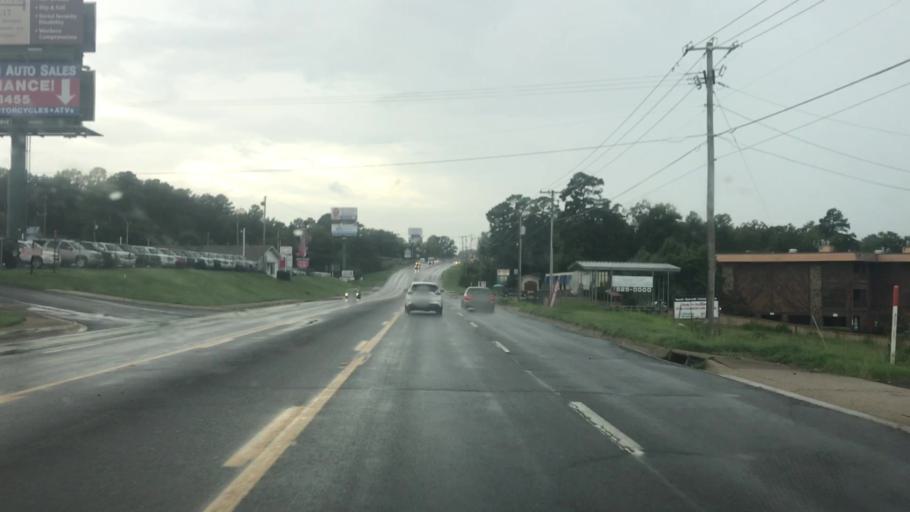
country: US
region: Arkansas
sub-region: Garland County
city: Rockwell
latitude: 34.4707
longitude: -93.1306
